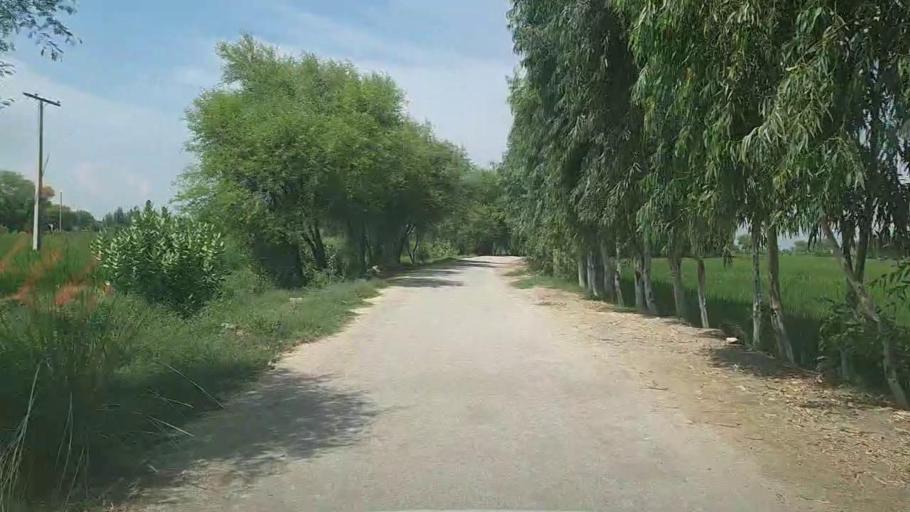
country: PK
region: Sindh
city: Kandhkot
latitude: 28.2986
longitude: 69.2359
